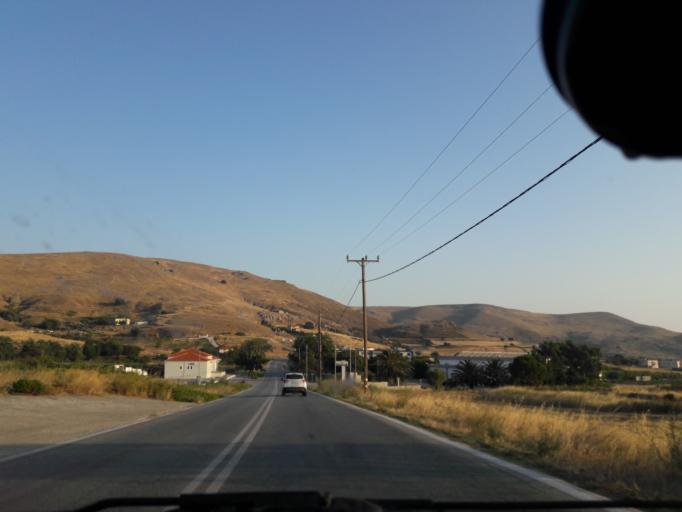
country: GR
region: North Aegean
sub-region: Nomos Lesvou
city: Myrina
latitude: 39.9087
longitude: 25.1120
